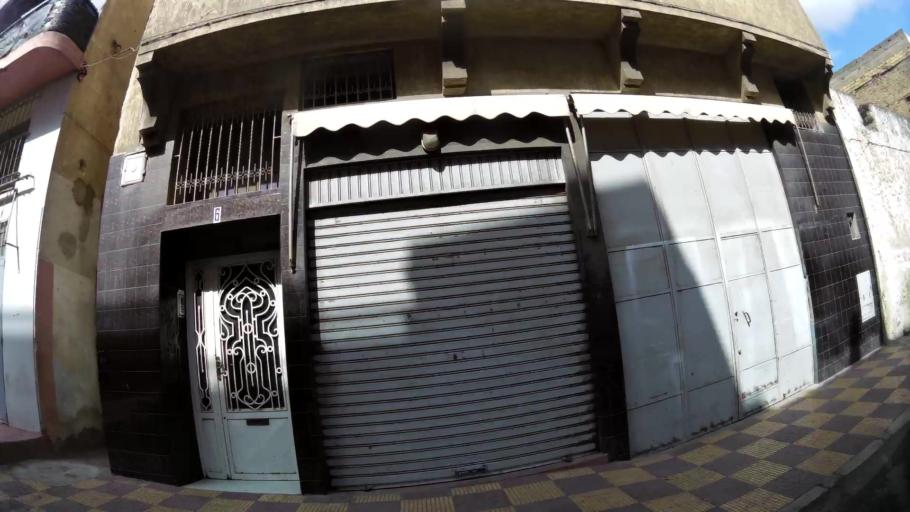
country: MA
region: Gharb-Chrarda-Beni Hssen
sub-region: Kenitra Province
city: Kenitra
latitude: 34.2636
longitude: -6.5678
